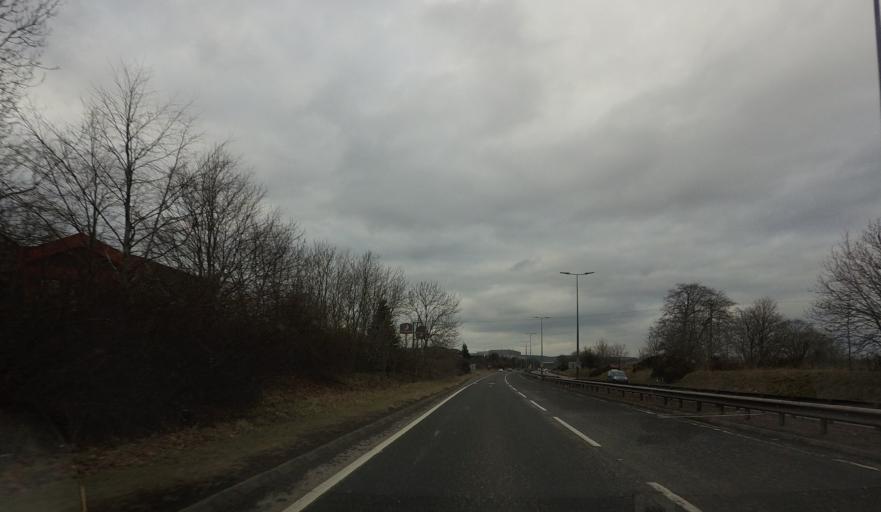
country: GB
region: Scotland
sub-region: Highland
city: Inverness
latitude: 57.4728
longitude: -4.1855
